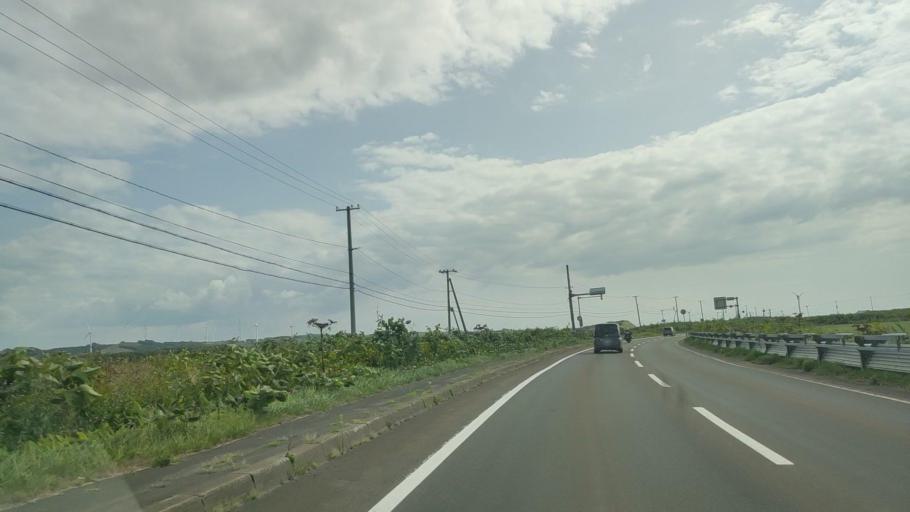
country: JP
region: Hokkaido
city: Rumoi
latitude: 44.2733
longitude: 141.6576
